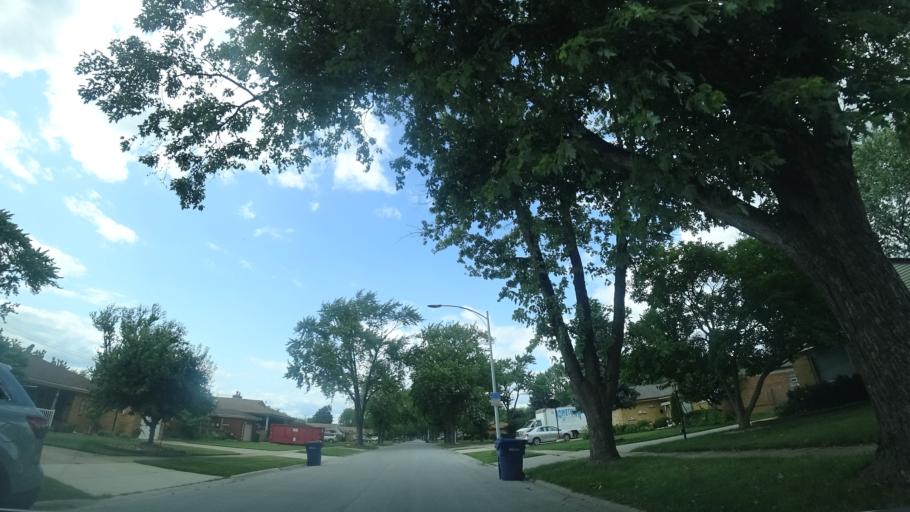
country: US
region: Illinois
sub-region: Cook County
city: Merrionette Park
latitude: 41.6930
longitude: -87.7247
